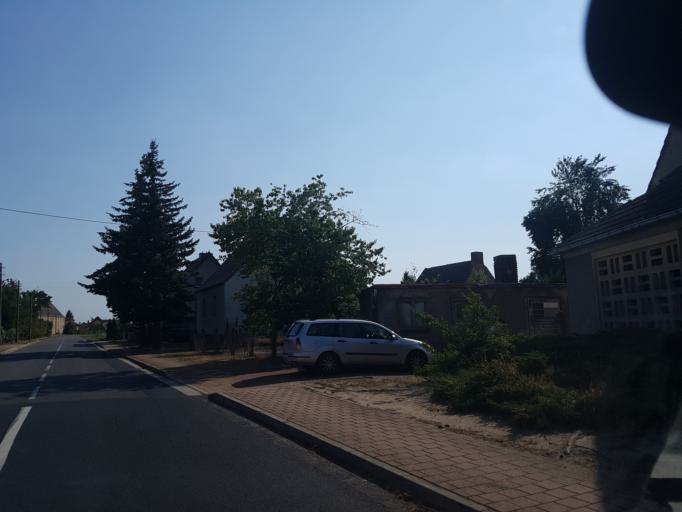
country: DE
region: Saxony-Anhalt
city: Annaburg
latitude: 51.6946
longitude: 12.9983
